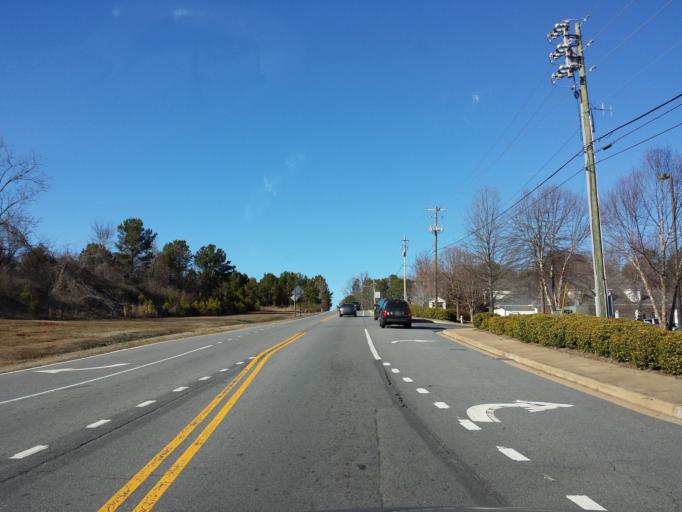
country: US
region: Georgia
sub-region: Cobb County
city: Kennesaw
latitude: 33.9533
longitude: -84.6616
